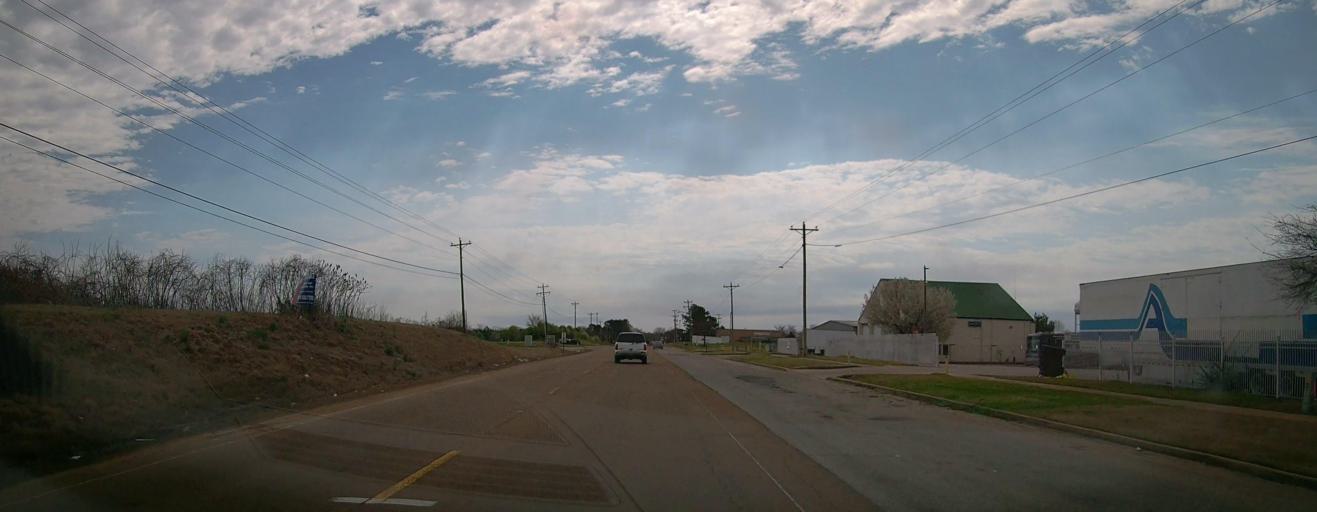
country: US
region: Mississippi
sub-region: De Soto County
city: Olive Branch
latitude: 34.9311
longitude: -89.7931
